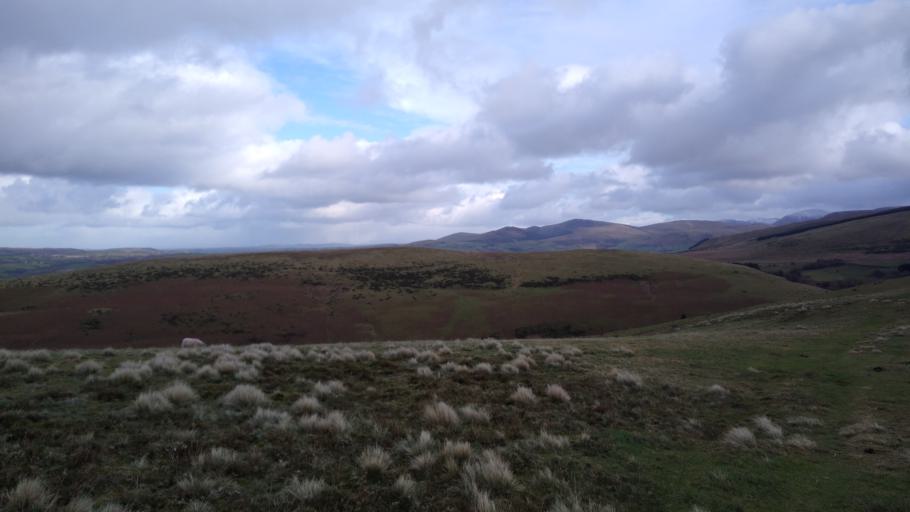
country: GB
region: England
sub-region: Cumbria
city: Frizington
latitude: 54.5010
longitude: -3.4725
